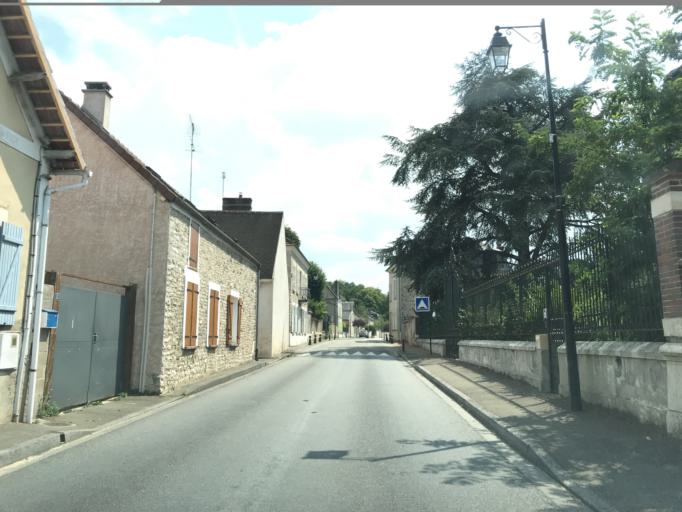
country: FR
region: Haute-Normandie
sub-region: Departement de l'Eure
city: Breuilpont
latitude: 48.9617
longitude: 1.4276
